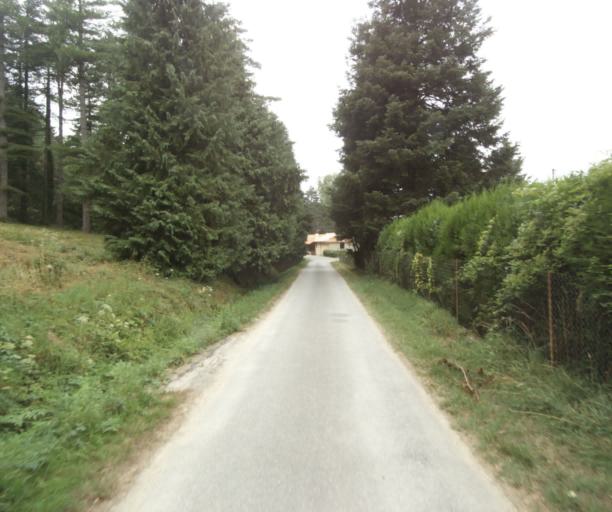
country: FR
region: Midi-Pyrenees
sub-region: Departement du Tarn
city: Soreze
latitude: 43.4333
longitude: 2.0408
